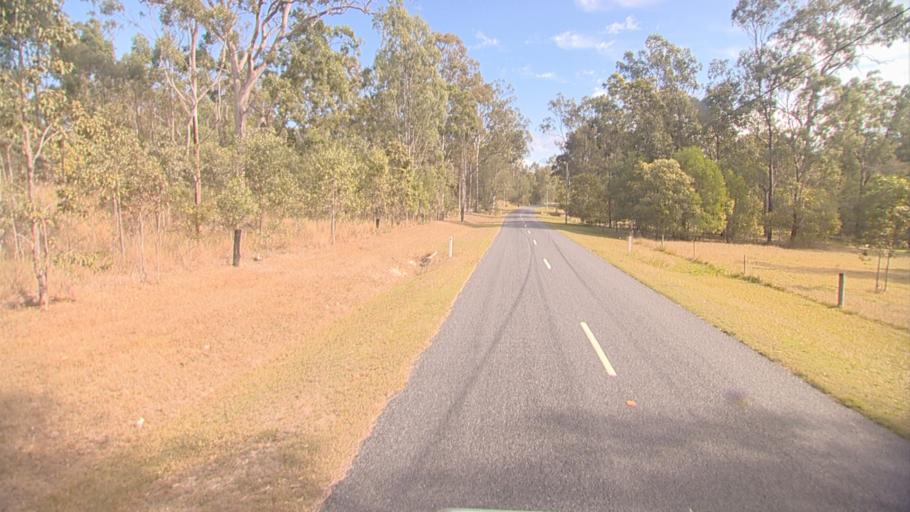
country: AU
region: Queensland
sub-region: Logan
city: North Maclean
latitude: -27.7615
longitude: 152.9745
